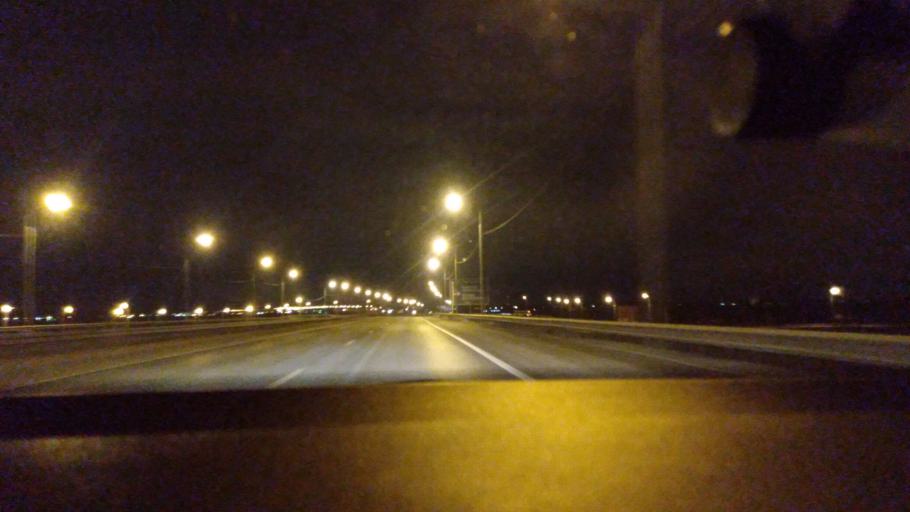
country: RU
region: Moskovskaya
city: Kolomna
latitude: 55.1309
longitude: 38.7798
